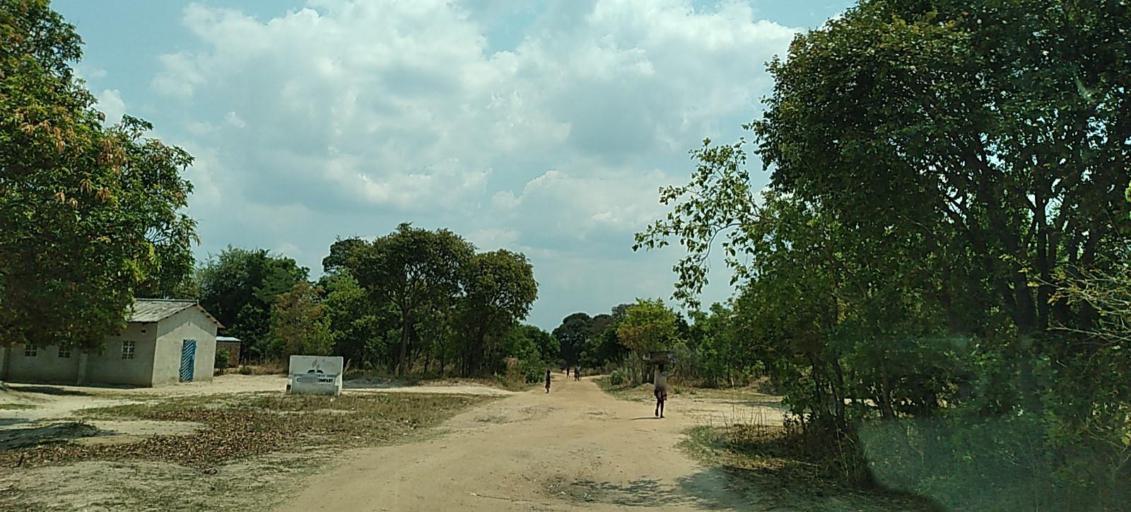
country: ZM
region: Copperbelt
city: Luanshya
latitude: -13.1583
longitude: 28.3100
